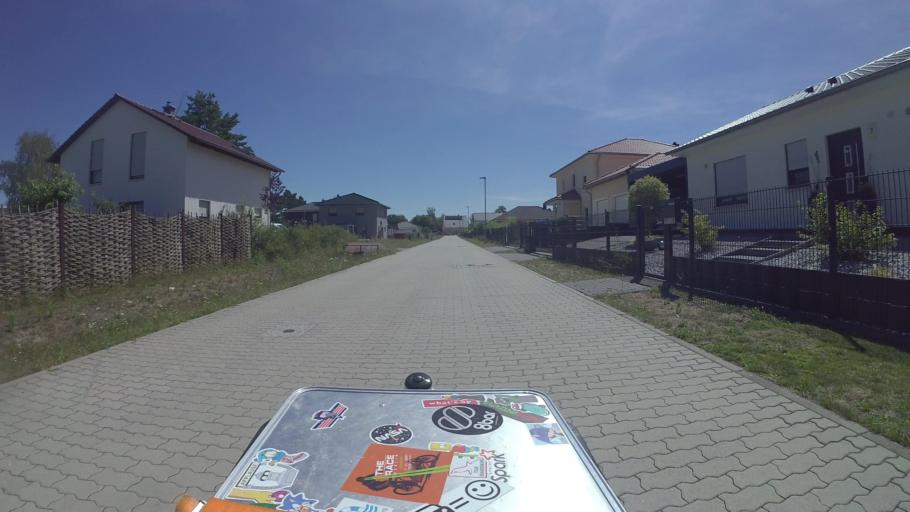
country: DE
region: Brandenburg
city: Sperenberg
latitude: 52.1639
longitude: 13.3711
